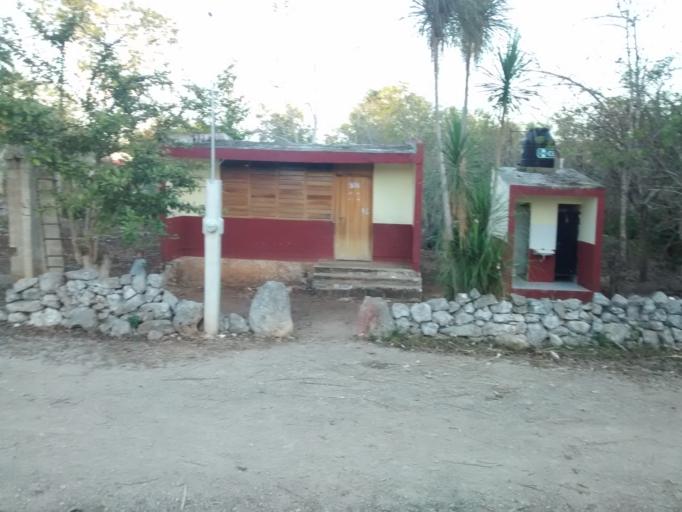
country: MX
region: Yucatan
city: Chichimila
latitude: 20.4469
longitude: -88.1980
